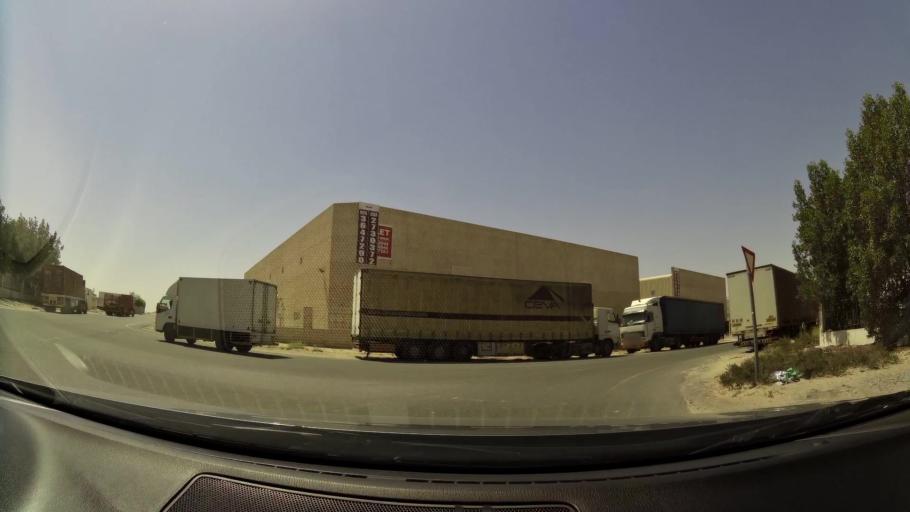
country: AE
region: Dubai
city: Dubai
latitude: 24.9763
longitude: 55.2091
